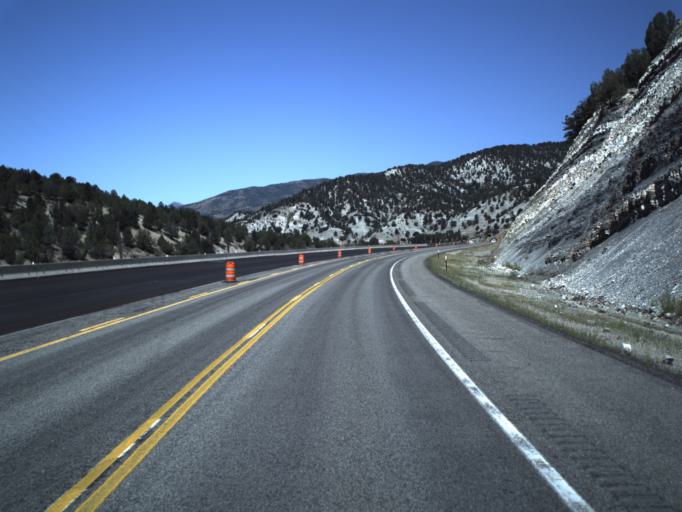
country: US
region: Utah
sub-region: Utah County
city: Mapleton
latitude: 39.9578
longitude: -111.3019
